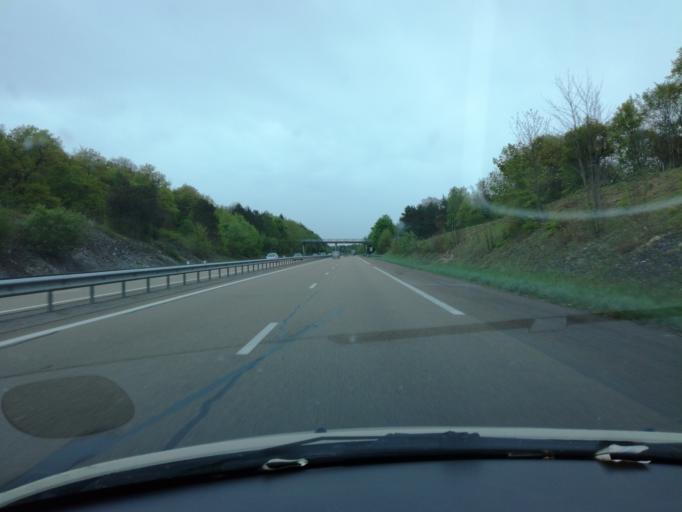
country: FR
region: Champagne-Ardenne
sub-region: Departement de la Haute-Marne
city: Chamarandes-Choignes
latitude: 48.0209
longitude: 5.0944
